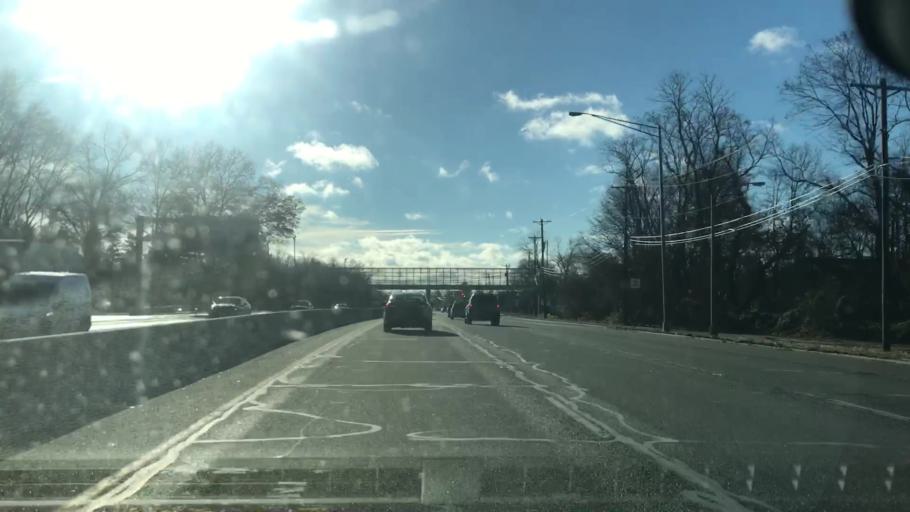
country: US
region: New Jersey
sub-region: Bergen County
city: Ho-Ho-Kus
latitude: 40.9929
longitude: -74.0962
